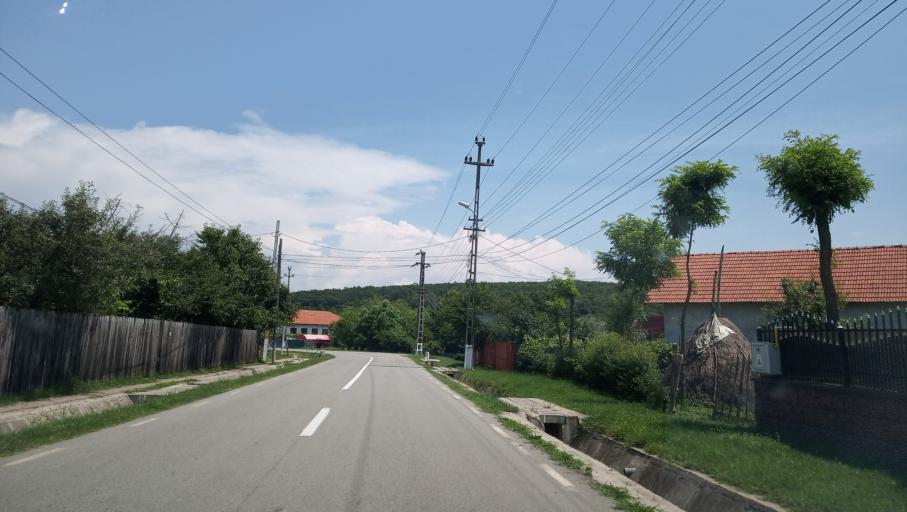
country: RO
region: Gorj
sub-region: Comuna Turcinesti
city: Turcinesti
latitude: 45.0473
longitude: 23.3453
